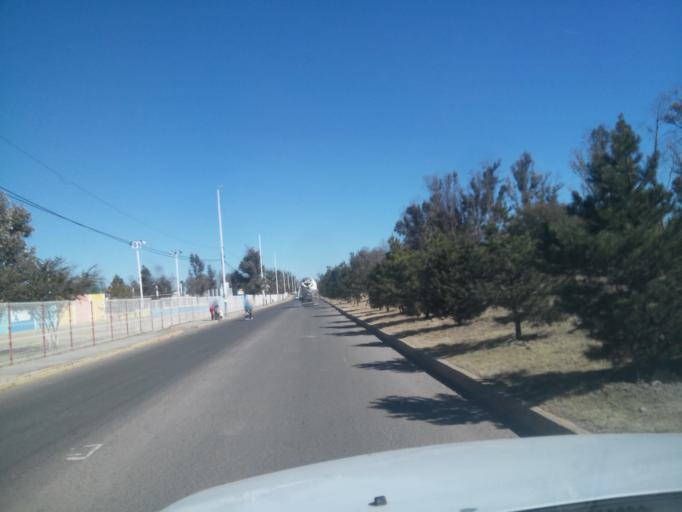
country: MX
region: Durango
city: Victoria de Durango
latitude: 24.0219
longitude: -104.6998
